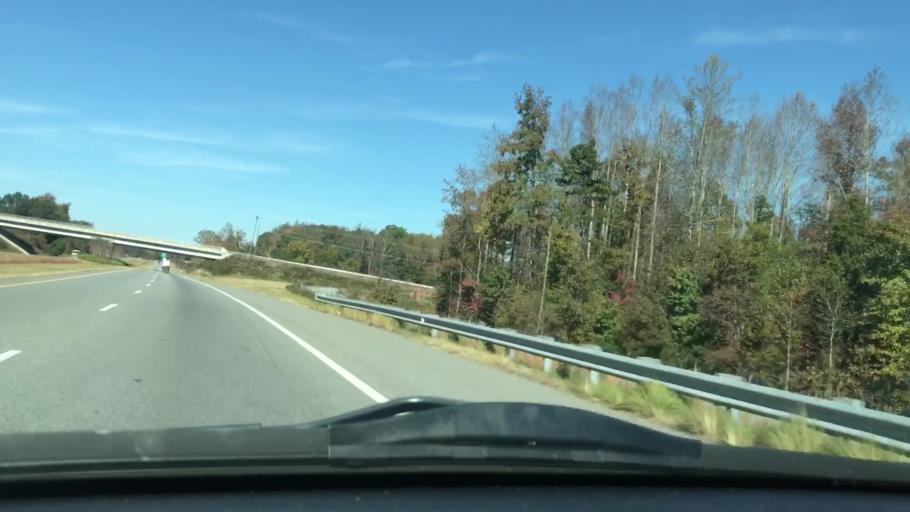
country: US
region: North Carolina
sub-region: Randolph County
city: Archdale
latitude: 35.9015
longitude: -79.9109
